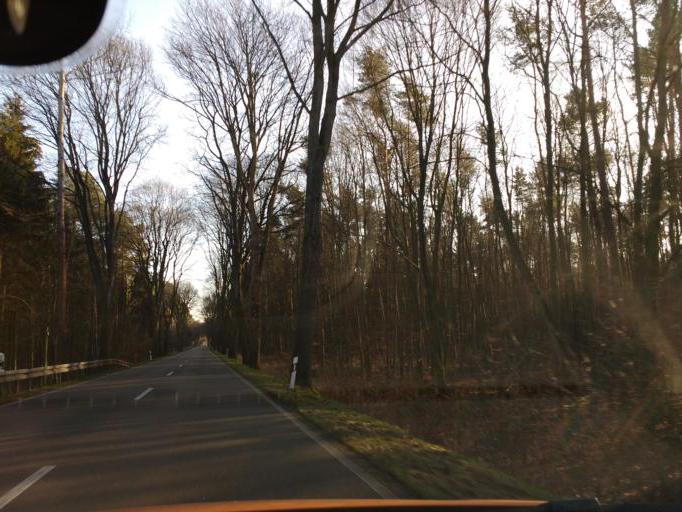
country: DE
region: Brandenburg
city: Strausberg
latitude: 52.6545
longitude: 13.8924
